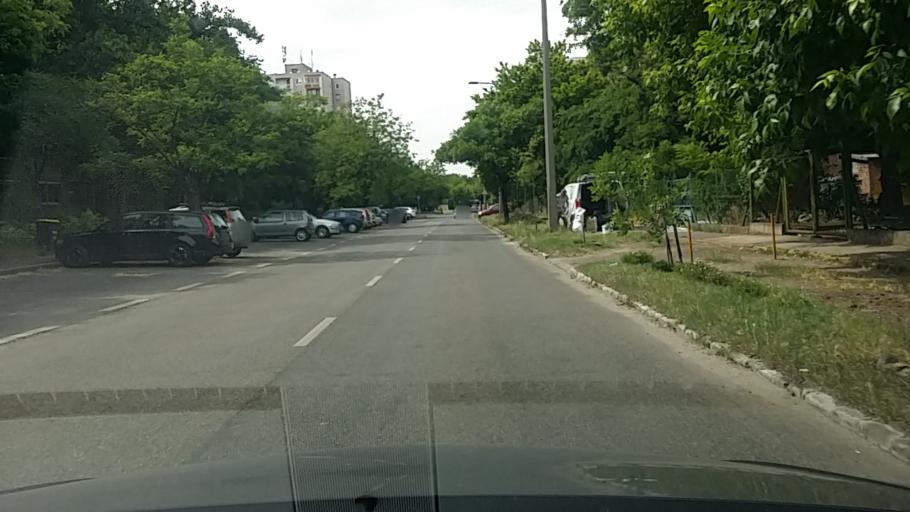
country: HU
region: Budapest
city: Budapest XXI. keruelet
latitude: 47.4180
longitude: 19.0684
